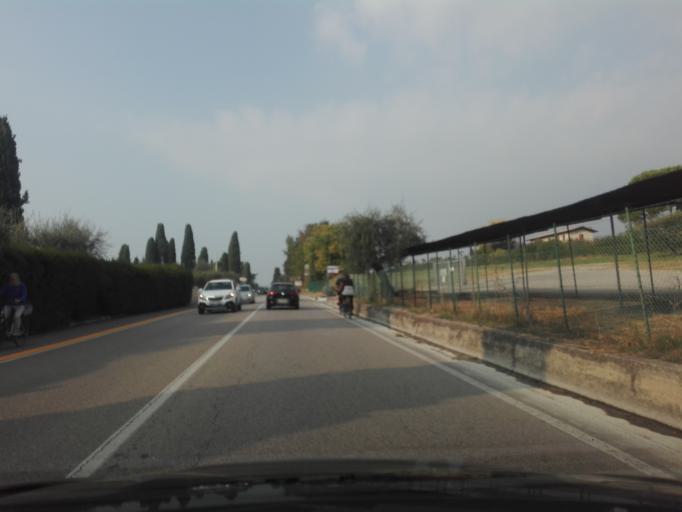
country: IT
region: Veneto
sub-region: Provincia di Verona
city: Lazise
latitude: 45.5161
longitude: 10.7311
